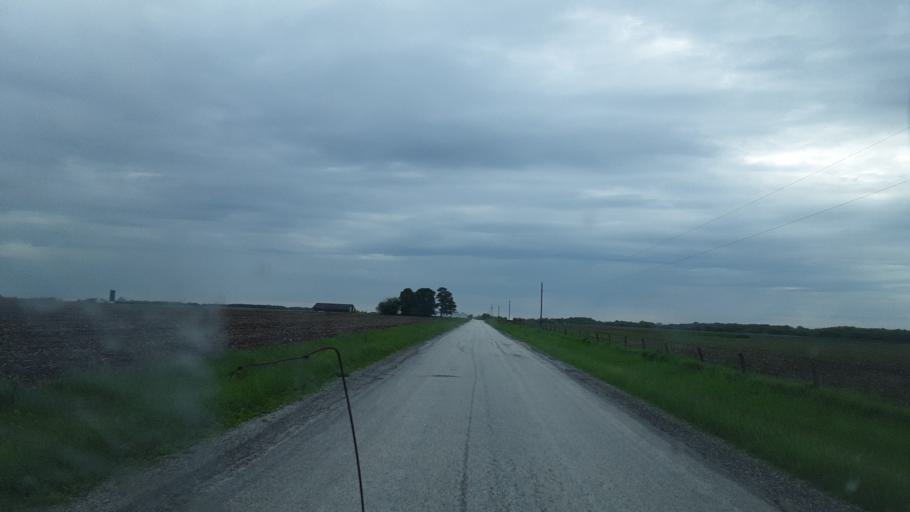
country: US
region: Illinois
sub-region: McDonough County
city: Macomb
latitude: 40.3818
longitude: -90.6367
